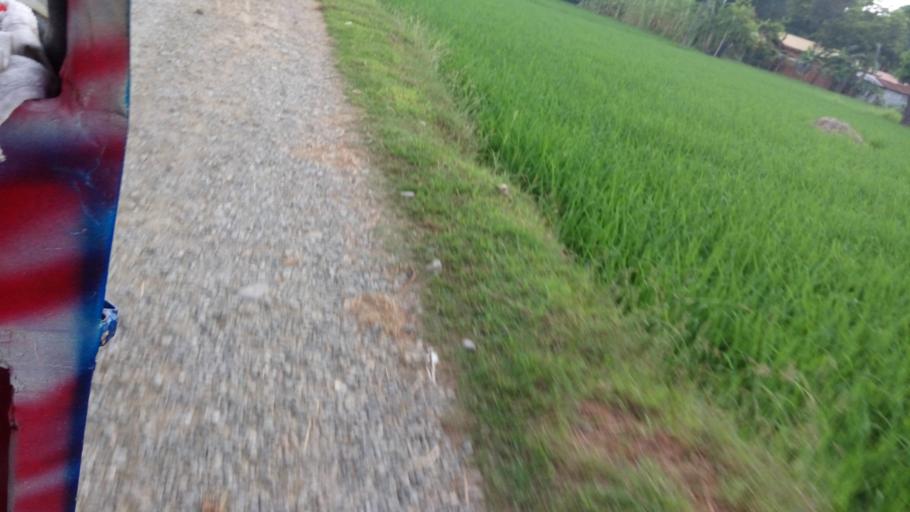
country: PH
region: Ilocos
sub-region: Province of La Union
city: Santo Tomas
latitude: 16.2875
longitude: 120.3816
